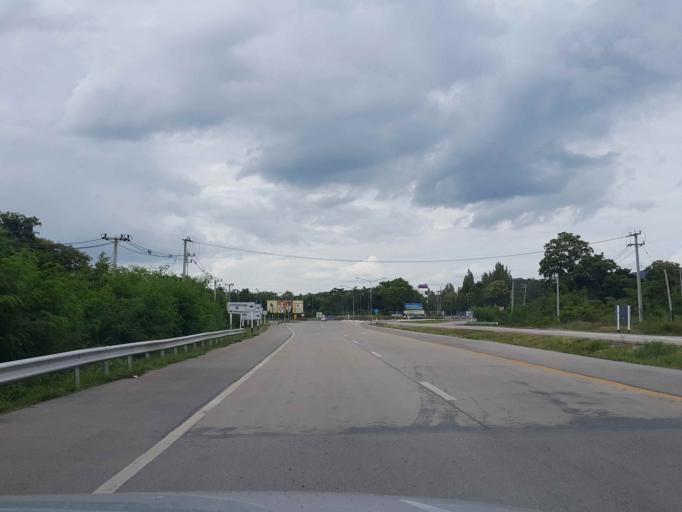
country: TH
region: Lampang
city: Lampang
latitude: 18.2552
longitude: 99.5397
